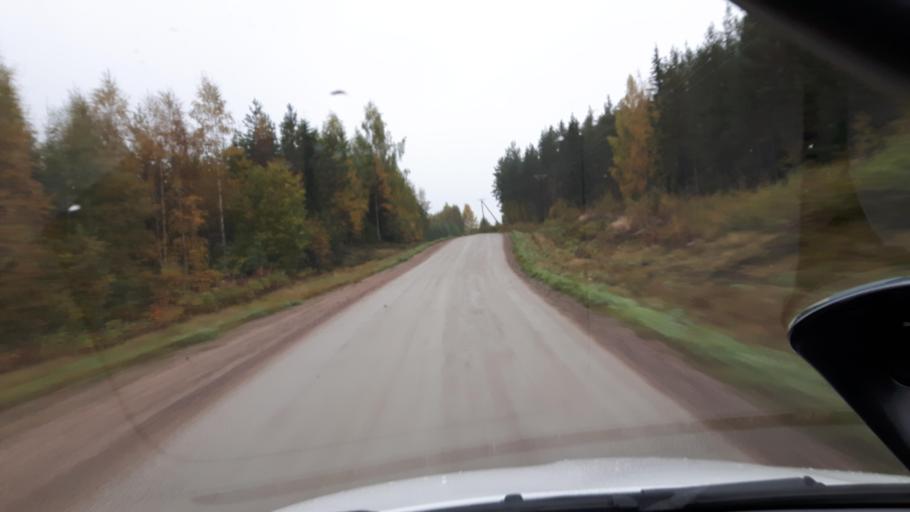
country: SE
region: Vaesternorrland
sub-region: Ange Kommun
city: Ange
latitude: 62.1572
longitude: 15.6623
